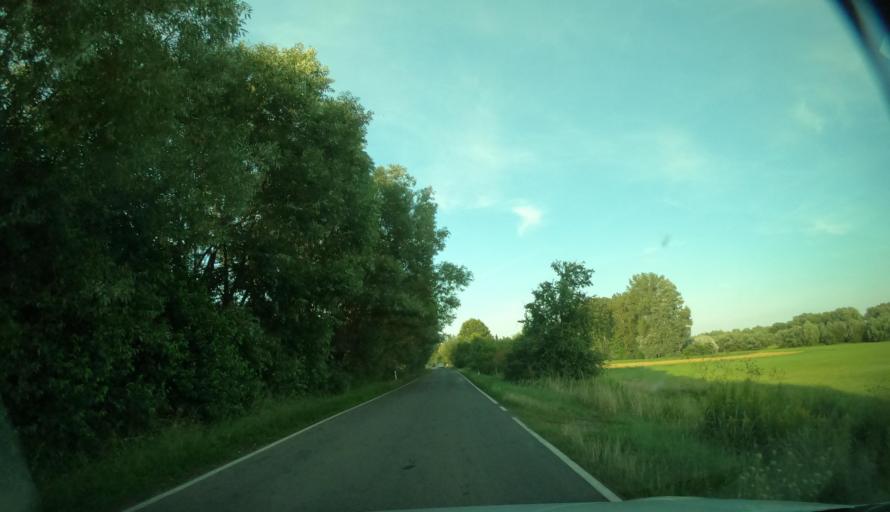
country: PL
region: Kujawsko-Pomorskie
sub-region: Bydgoszcz
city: Fordon
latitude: 53.2275
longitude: 18.1989
